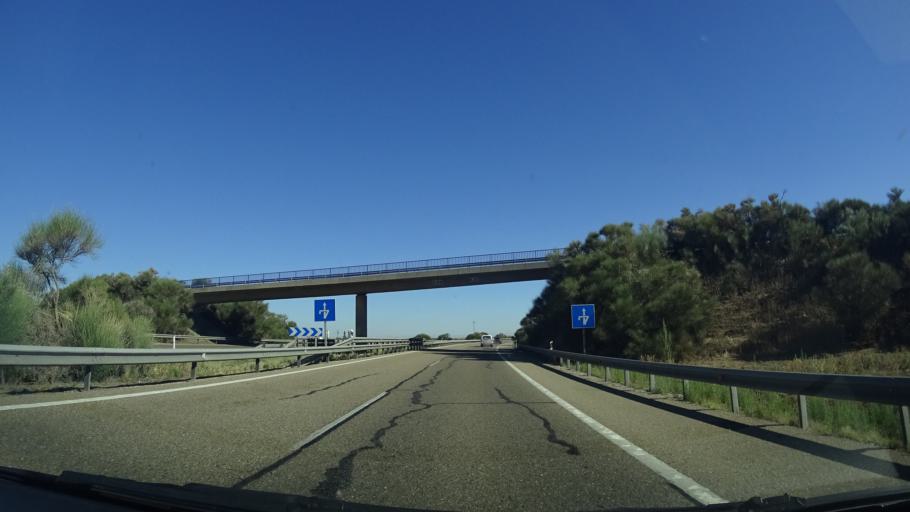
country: ES
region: Castille and Leon
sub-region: Provincia de Valladolid
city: Villardefrades
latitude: 41.7200
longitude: -5.2475
